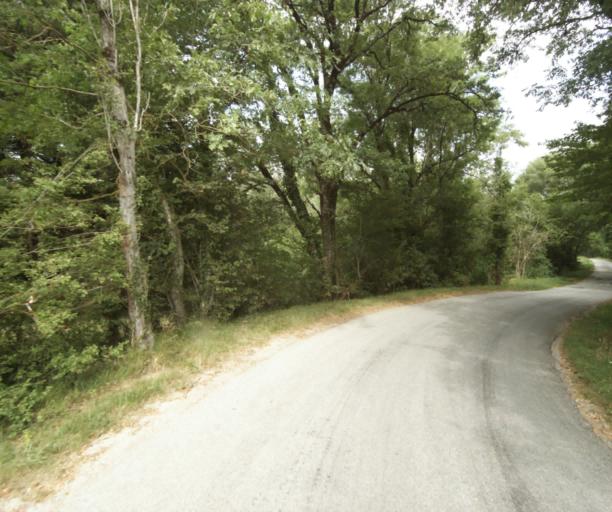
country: FR
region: Midi-Pyrenees
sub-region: Departement du Tarn
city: Soreze
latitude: 43.4375
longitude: 2.0392
